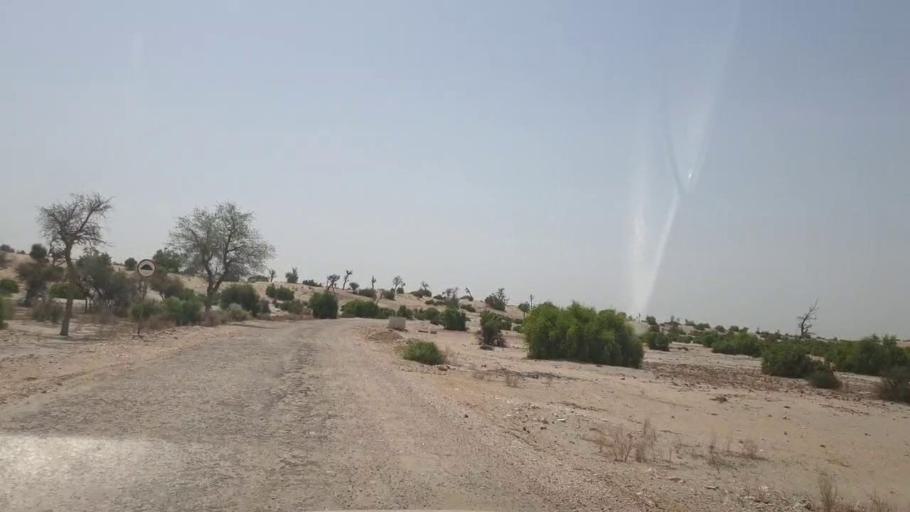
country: PK
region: Sindh
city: Khanpur
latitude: 27.3581
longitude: 69.3170
